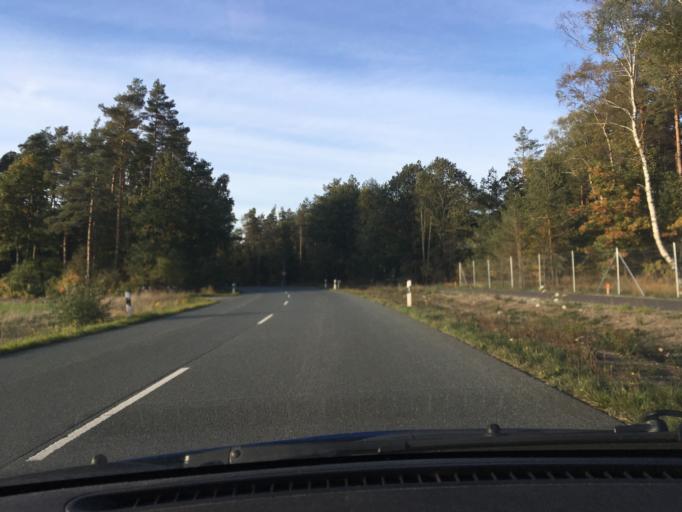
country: DE
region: Lower Saxony
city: Munster
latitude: 53.0417
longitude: 10.0586
